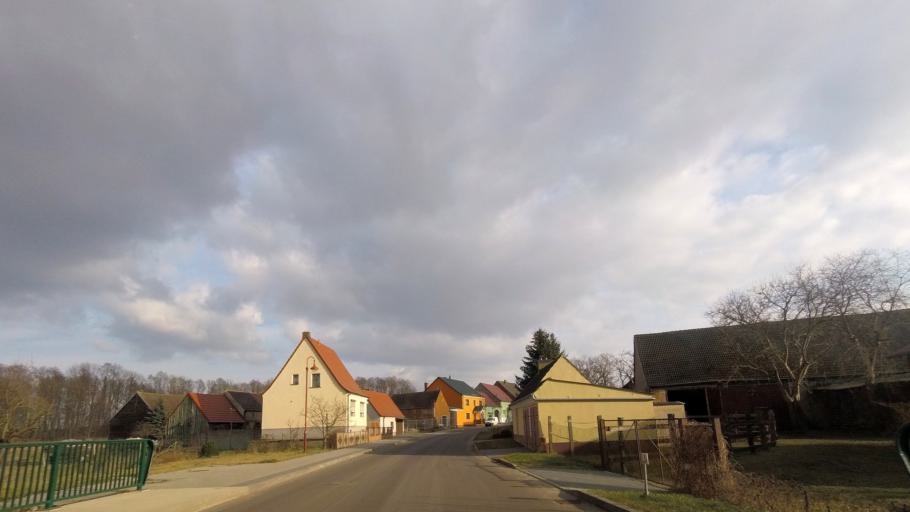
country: DE
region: Brandenburg
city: Belzig
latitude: 52.1730
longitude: 12.6769
